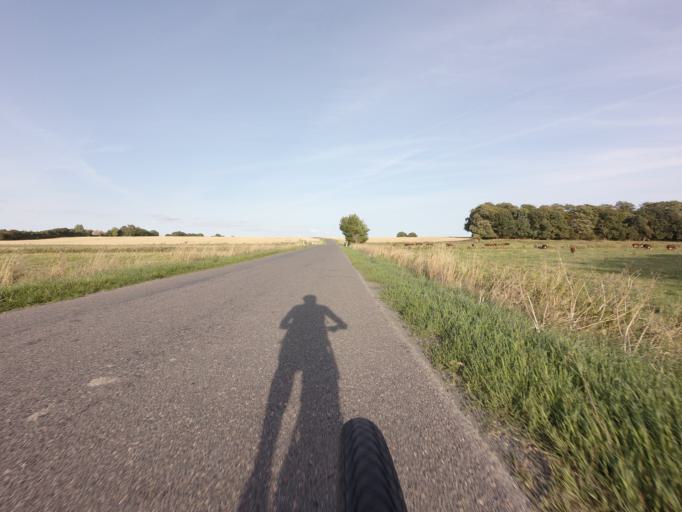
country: DK
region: Zealand
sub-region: Stevns Kommune
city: Store Heddinge
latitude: 55.2430
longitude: 12.3453
